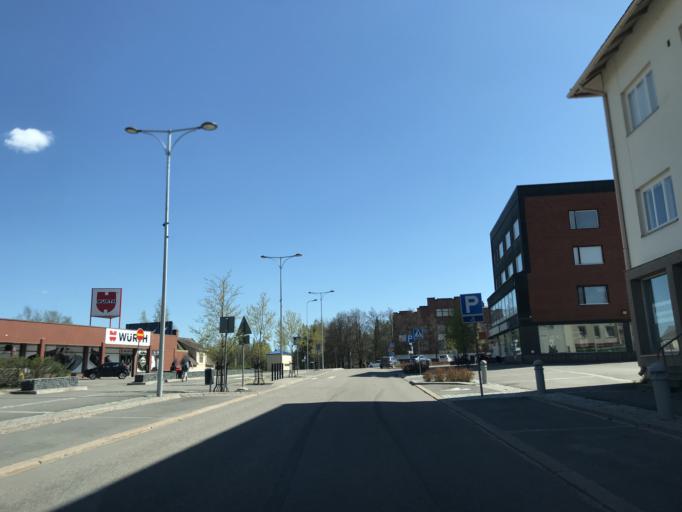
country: FI
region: Paijanne Tavastia
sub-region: Lahti
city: Orimattila
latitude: 60.8028
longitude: 25.7342
